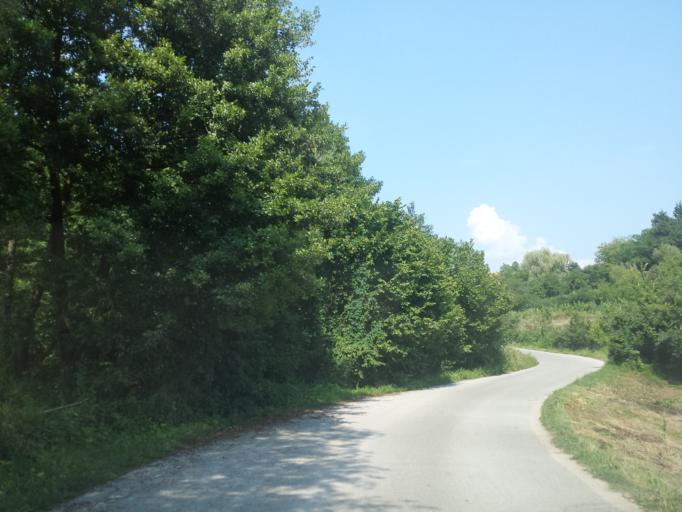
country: HR
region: Zagrebacka
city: Rude
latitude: 45.7228
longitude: 15.7033
